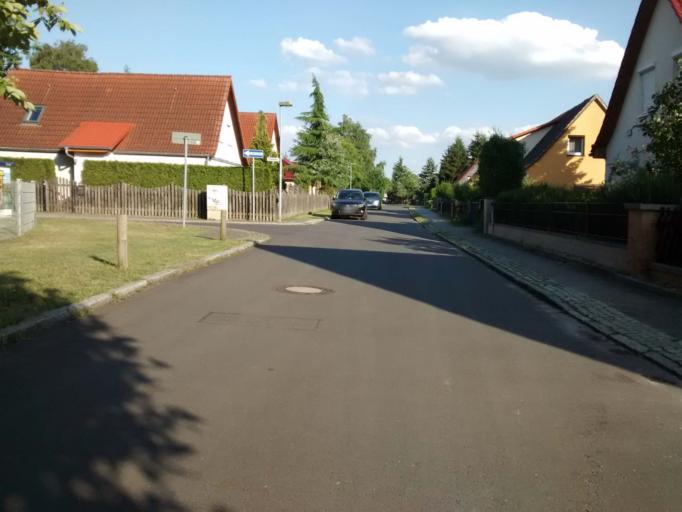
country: DE
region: Brandenburg
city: Hohen Neuendorf
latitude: 52.6615
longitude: 13.2734
